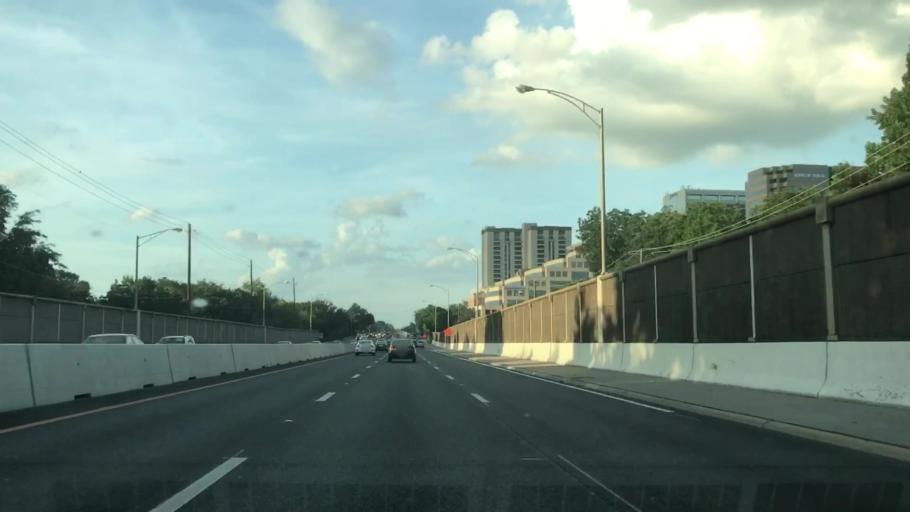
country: US
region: Texas
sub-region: Dallas County
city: University Park
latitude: 32.8588
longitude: -96.8122
